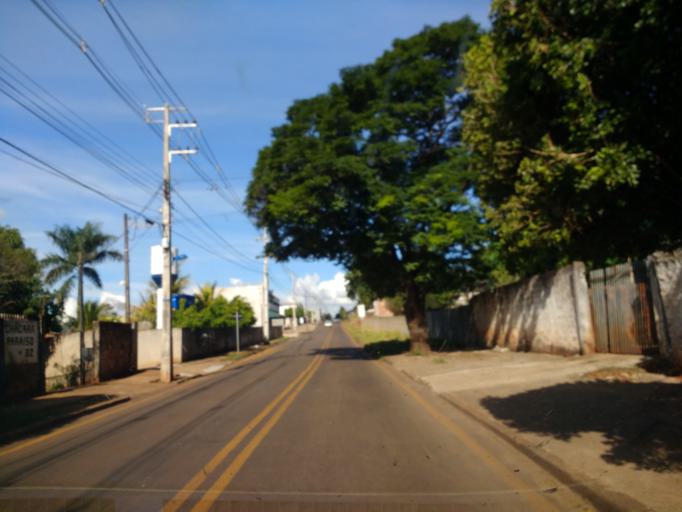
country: BR
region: Parana
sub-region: Maringa
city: Maringa
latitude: -23.4155
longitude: -51.9765
